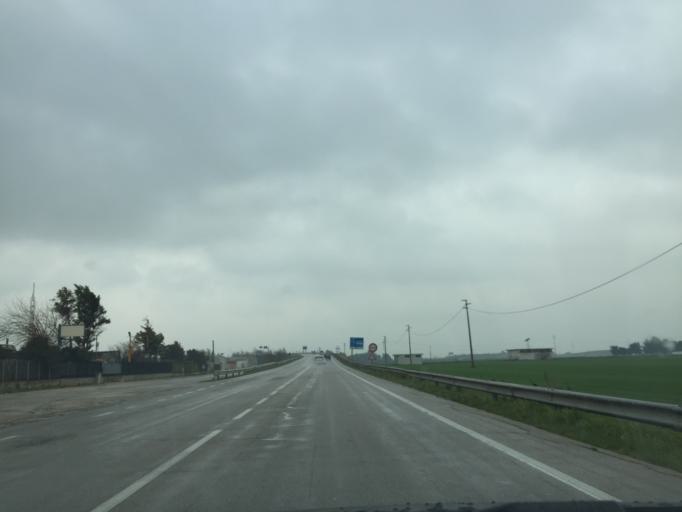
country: IT
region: Apulia
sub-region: Provincia di Foggia
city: Foggia
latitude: 41.4786
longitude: 15.5132
